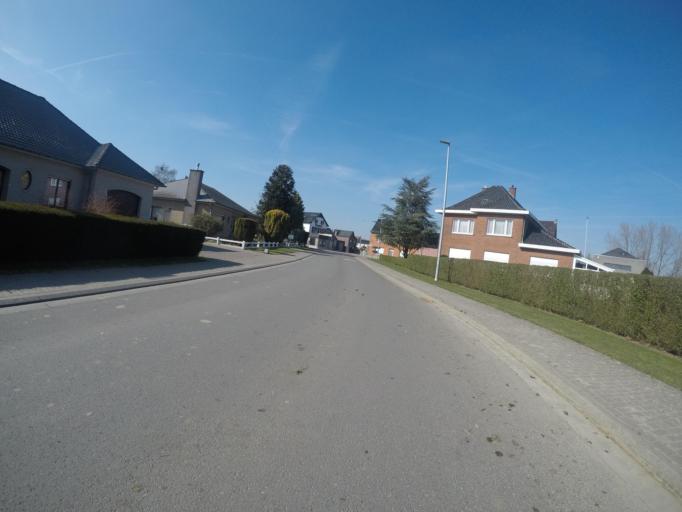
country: BE
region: Flanders
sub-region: Provincie Oost-Vlaanderen
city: Sint-Maria-Lierde
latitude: 50.8013
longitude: 3.8284
